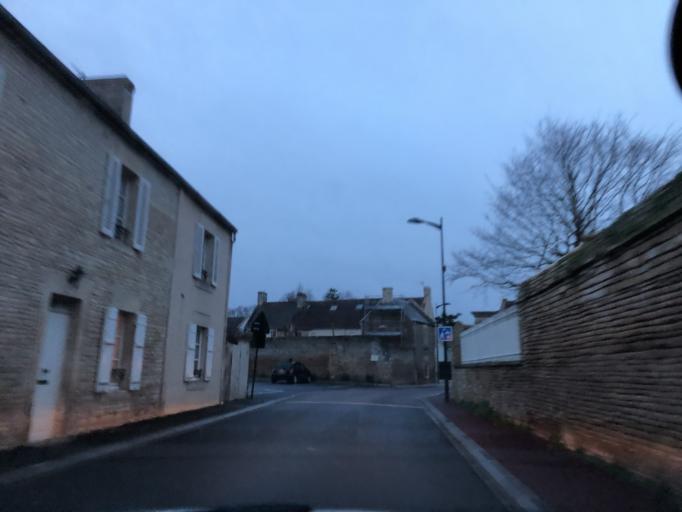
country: FR
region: Lower Normandy
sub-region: Departement du Calvados
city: Mathieu
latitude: 49.2511
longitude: -0.3657
